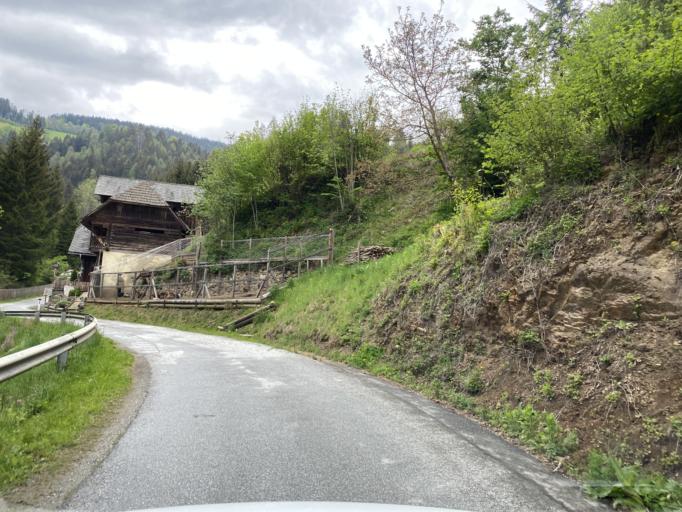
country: AT
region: Styria
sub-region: Politischer Bezirk Weiz
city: Koglhof
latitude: 47.3330
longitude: 15.6634
